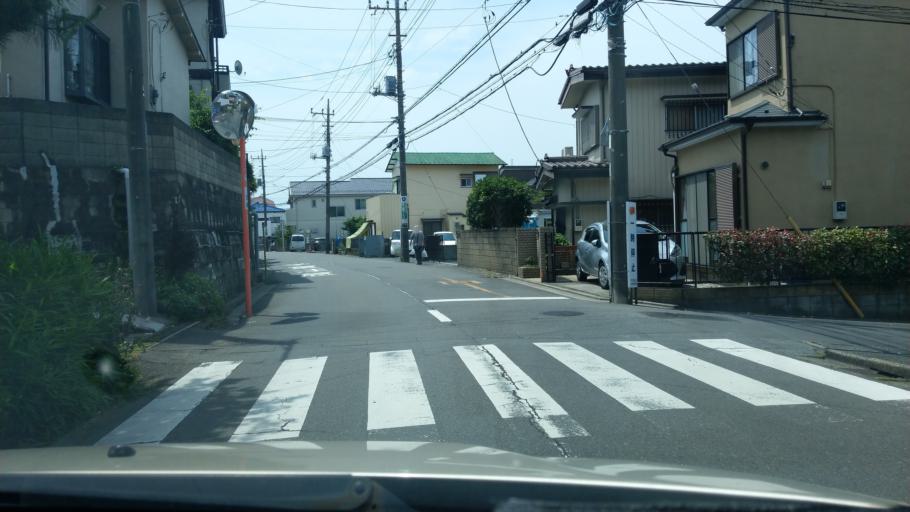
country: JP
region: Saitama
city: Saitama
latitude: 35.9106
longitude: 139.6493
